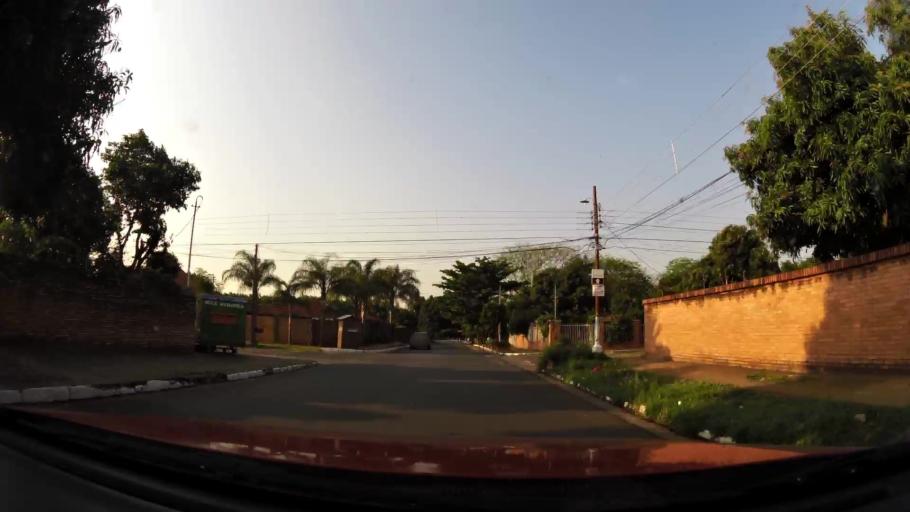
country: PY
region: Central
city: Lambare
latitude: -25.3503
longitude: -57.6097
